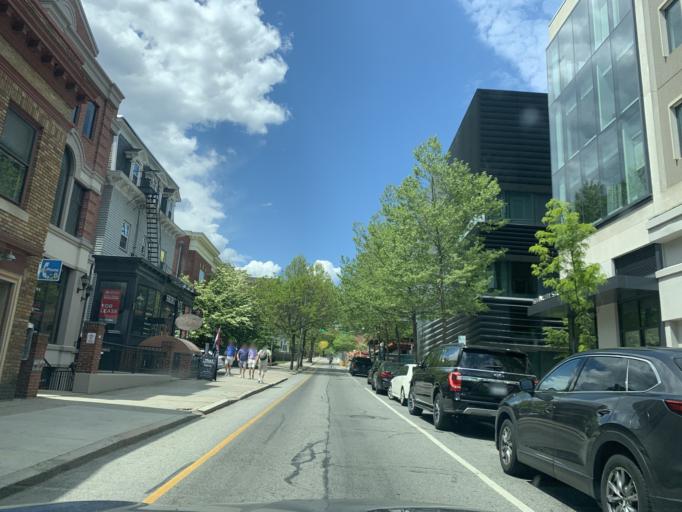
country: US
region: Rhode Island
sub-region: Providence County
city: Providence
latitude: 41.8280
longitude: -71.4009
